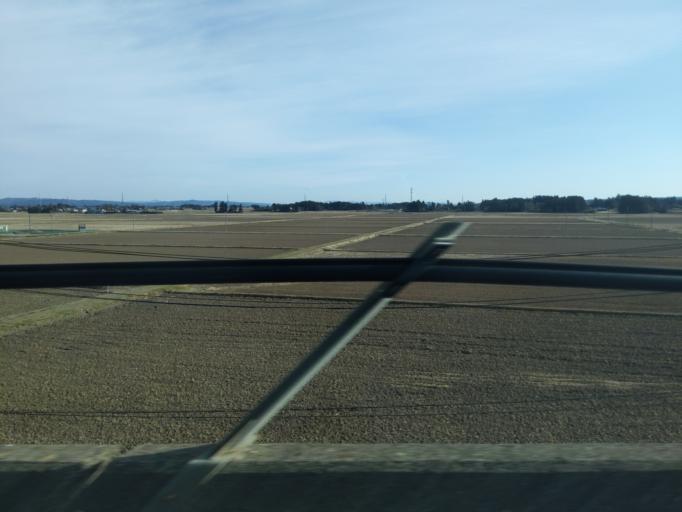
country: JP
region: Miyagi
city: Furukawa
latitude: 38.5474
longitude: 140.9619
